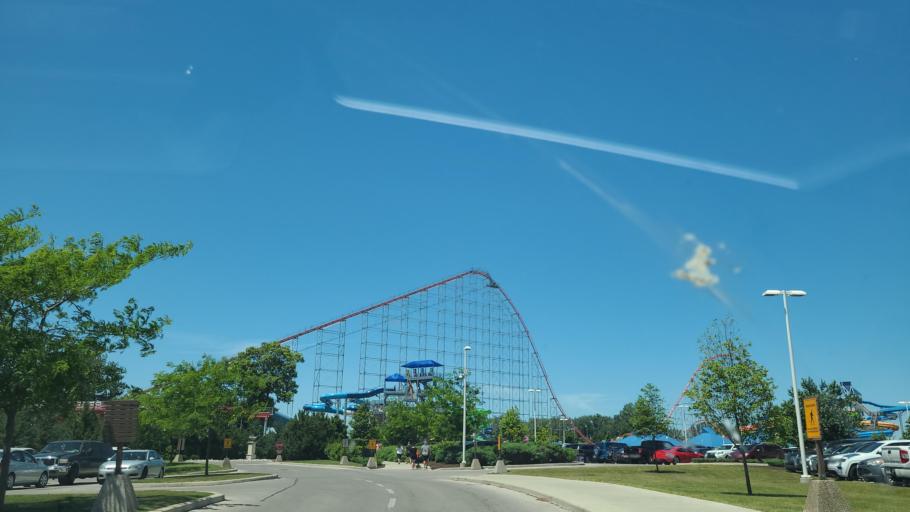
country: US
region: Ohio
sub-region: Erie County
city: Sandusky
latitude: 41.4857
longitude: -82.6845
